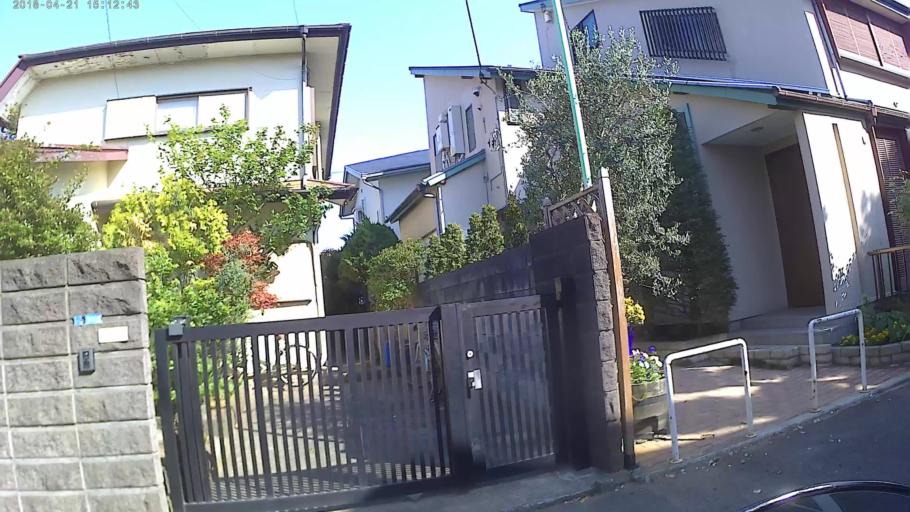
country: JP
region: Kanagawa
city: Fujisawa
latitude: 35.3202
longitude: 139.4665
